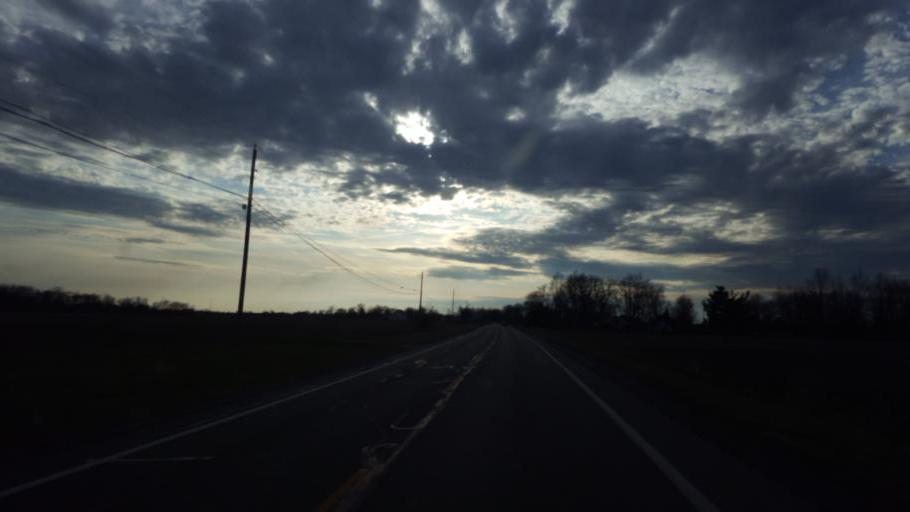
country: US
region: Ohio
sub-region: Morrow County
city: Cardington
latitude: 40.6312
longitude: -82.9769
